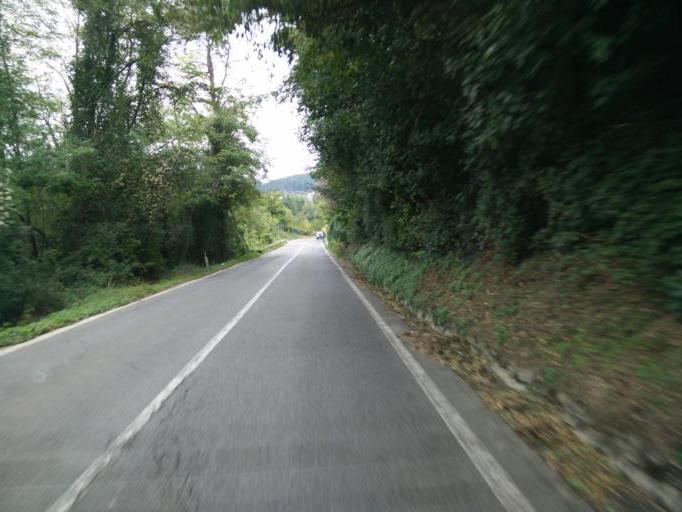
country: IT
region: Tuscany
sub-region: Provincia di Massa-Carrara
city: Fivizzano
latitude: 44.2311
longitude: 10.1198
